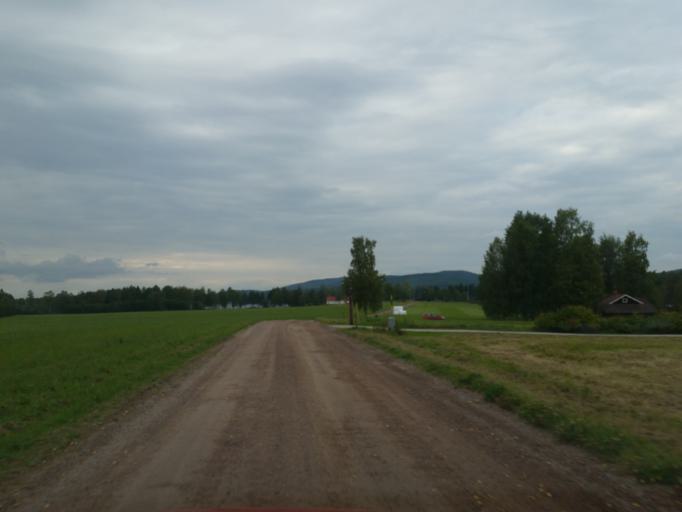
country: SE
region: Dalarna
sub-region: Leksand Municipality
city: Smedby
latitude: 60.6758
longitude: 15.1405
